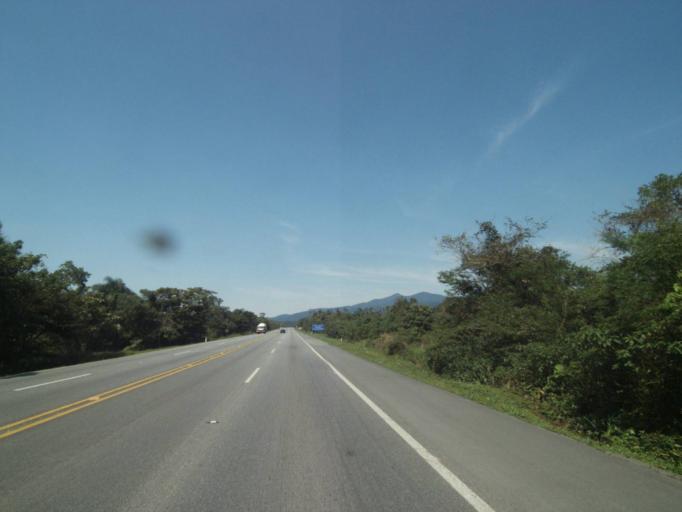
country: BR
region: Parana
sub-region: Paranagua
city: Paranagua
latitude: -25.5763
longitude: -48.6126
